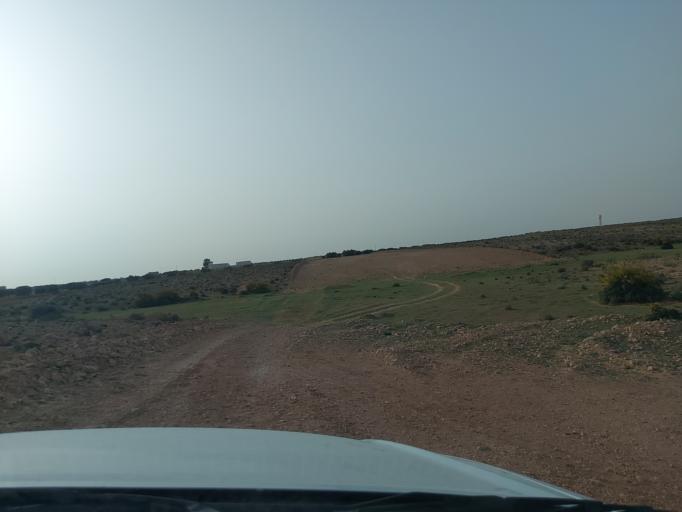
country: TN
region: Madanin
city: Medenine
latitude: 33.3388
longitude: 10.5943
